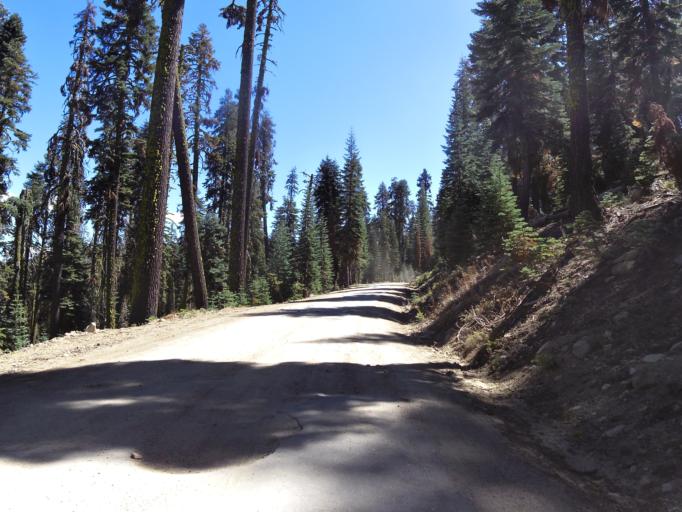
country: US
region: California
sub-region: Madera County
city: Oakhurst
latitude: 37.4225
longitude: -119.5012
